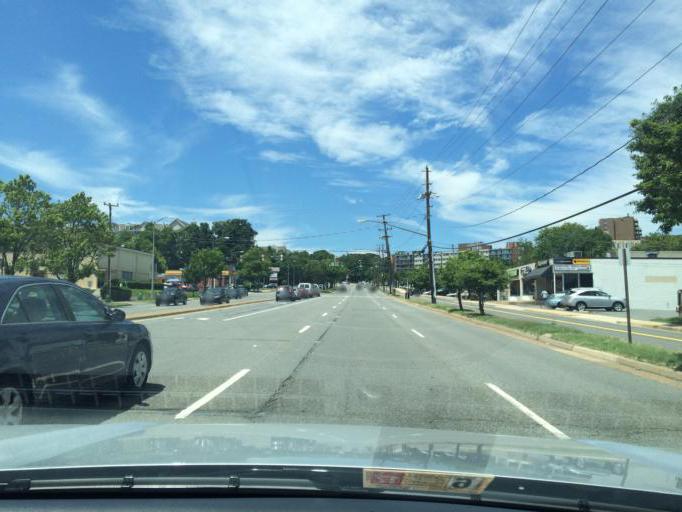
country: US
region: Virginia
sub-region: Fairfax County
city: Lincolnia
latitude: 38.8123
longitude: -77.1203
